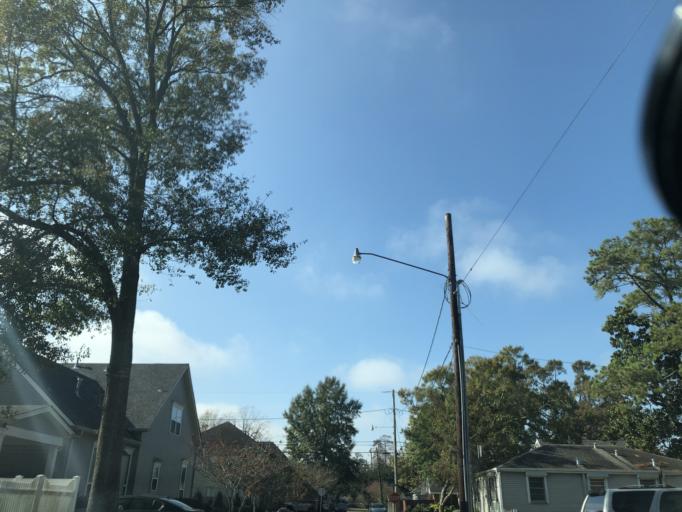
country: US
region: Louisiana
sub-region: Jefferson Parish
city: Metairie
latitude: 29.9859
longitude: -90.1514
